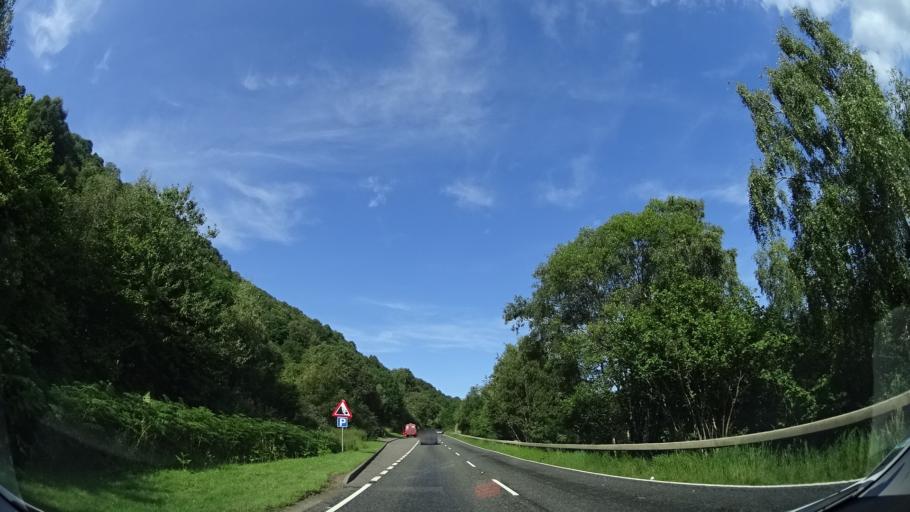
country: GB
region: Scotland
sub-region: Highland
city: Beauly
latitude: 57.3075
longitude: -4.4637
